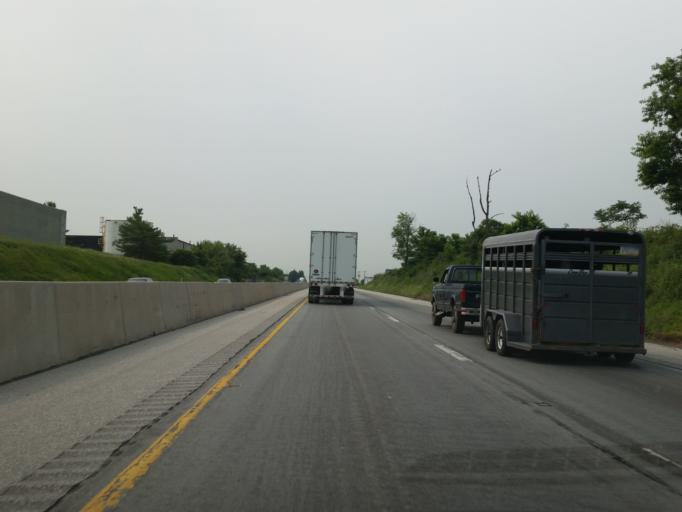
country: US
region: Pennsylvania
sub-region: York County
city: Emigsville
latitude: 40.0348
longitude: -76.7468
